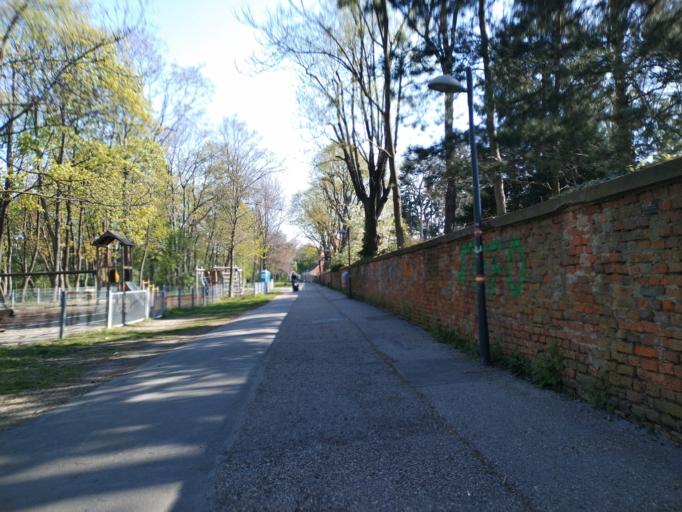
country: AT
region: Lower Austria
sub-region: Politischer Bezirk Modling
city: Vosendorf
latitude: 48.1651
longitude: 16.3064
